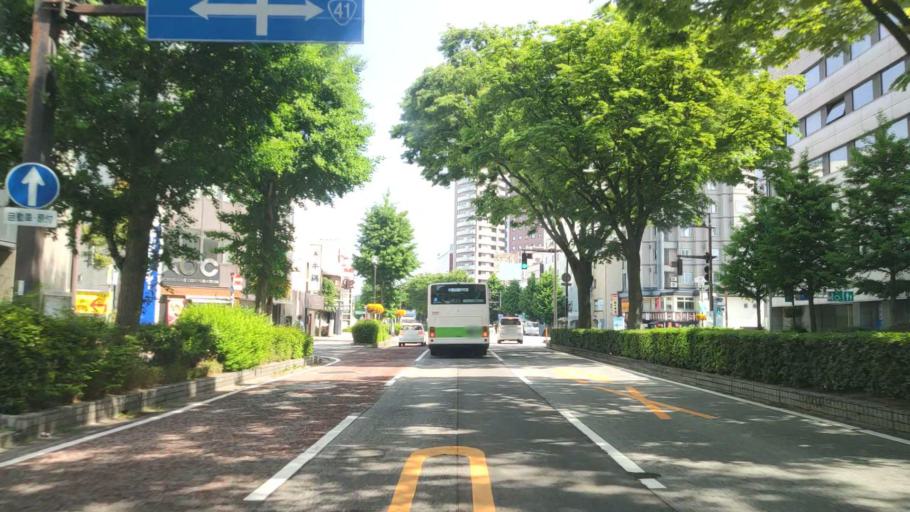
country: JP
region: Toyama
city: Toyama-shi
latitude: 36.6972
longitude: 137.2131
